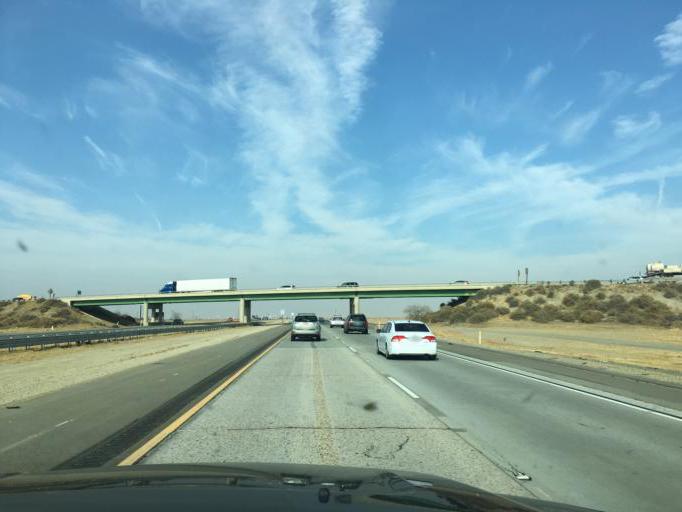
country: US
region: California
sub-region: Kern County
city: Lost Hills
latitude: 35.6150
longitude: -119.6522
